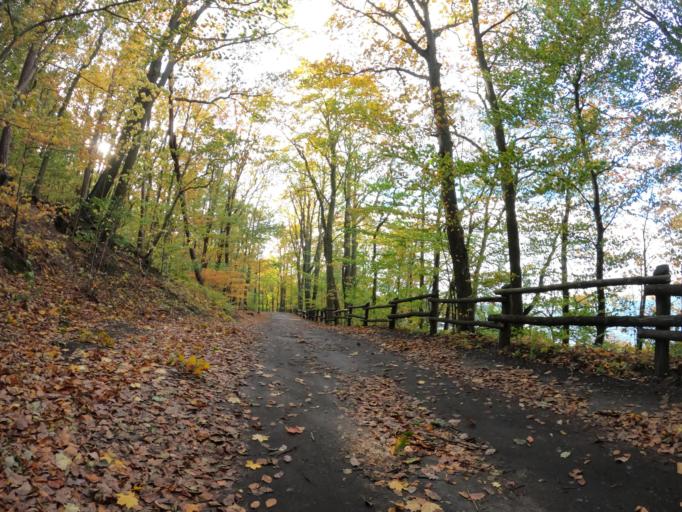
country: PL
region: West Pomeranian Voivodeship
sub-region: Powiat mysliborski
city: Barlinek
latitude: 52.9815
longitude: 15.2274
